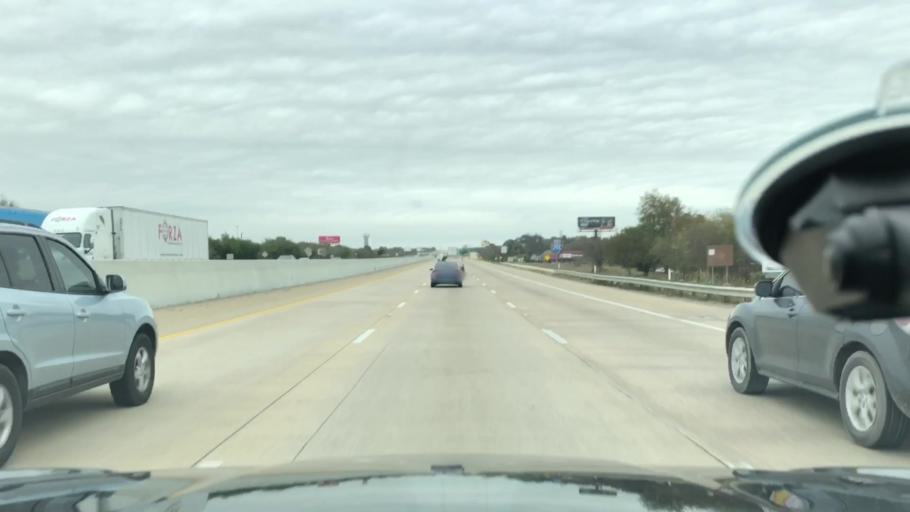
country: US
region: Texas
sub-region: Ellis County
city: Red Oak
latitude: 32.5051
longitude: -96.8220
